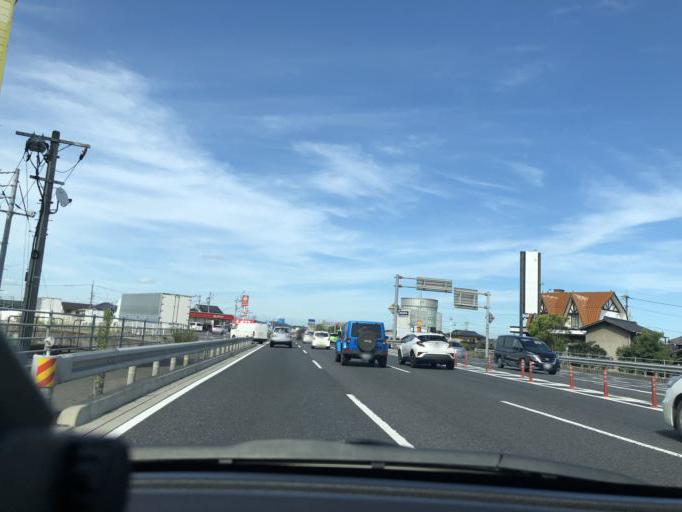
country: JP
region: Okayama
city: Kurashiki
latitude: 34.5904
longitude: 133.7970
